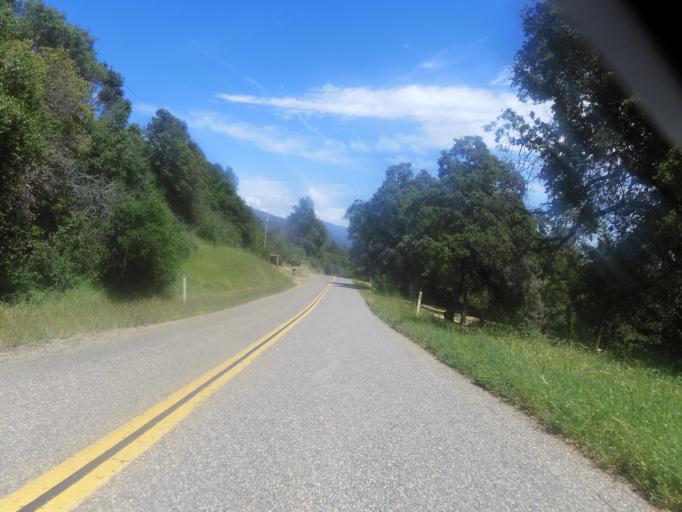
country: US
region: California
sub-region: Mariposa County
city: Midpines
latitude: 37.5119
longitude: -119.9035
